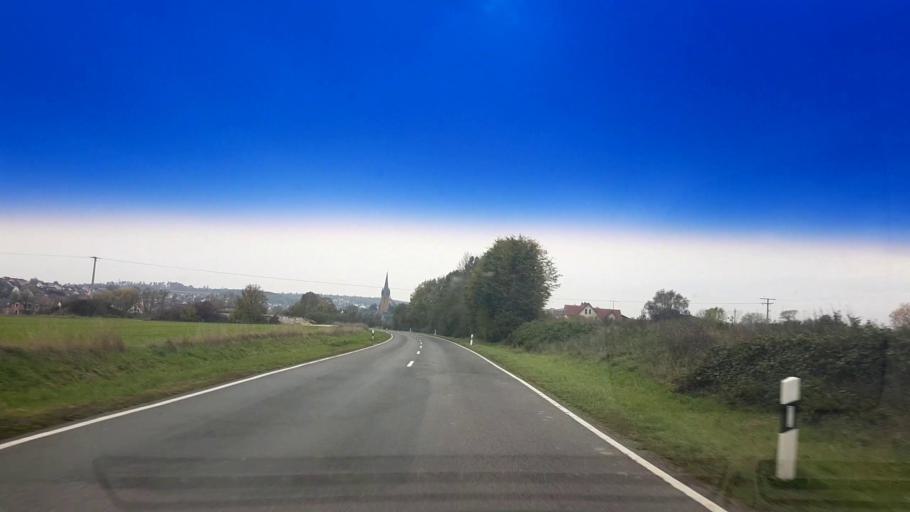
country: DE
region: Bavaria
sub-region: Upper Franconia
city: Litzendorf
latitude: 49.9158
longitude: 11.0200
